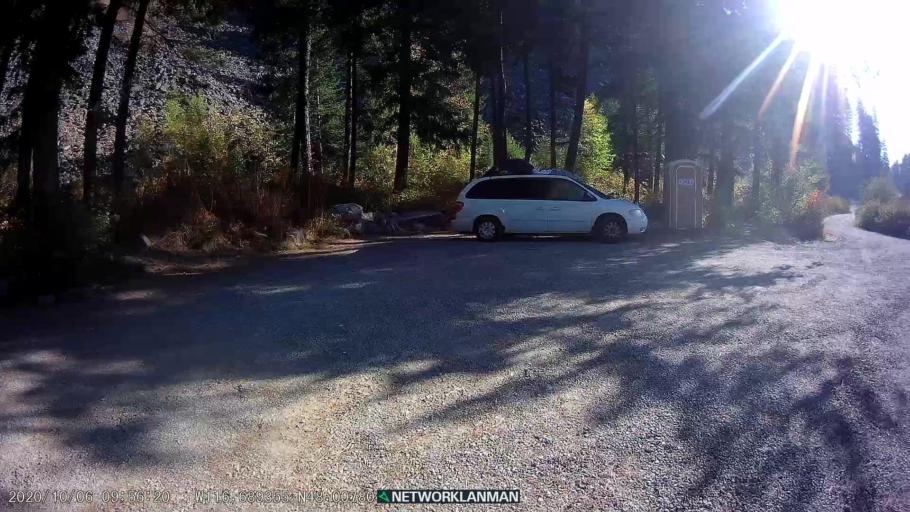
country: US
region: Idaho
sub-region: Kootenai County
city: Spirit Lake
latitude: 48.0063
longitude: -116.6882
